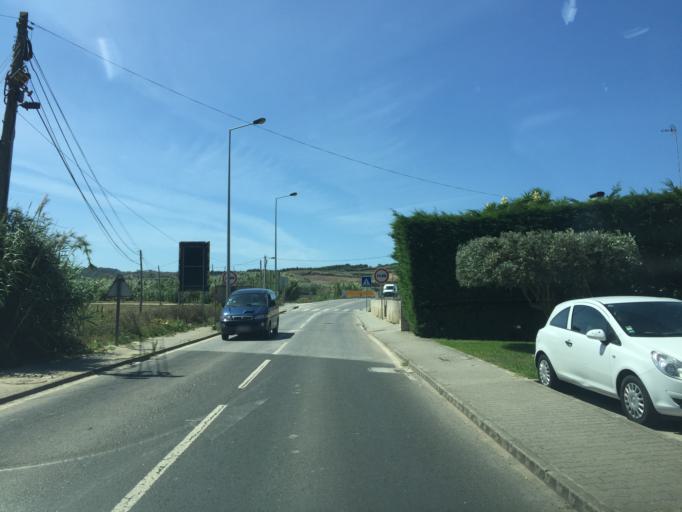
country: PT
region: Lisbon
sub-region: Lourinha
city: Lourinha
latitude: 39.2356
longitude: -9.3130
